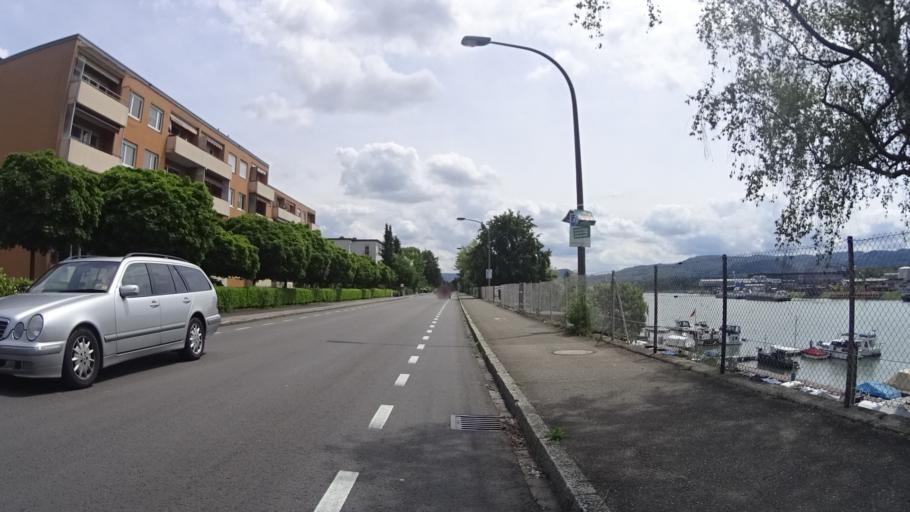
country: CH
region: Basel-Landschaft
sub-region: Bezirk Arlesheim
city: Birsfelden
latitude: 47.5603
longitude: 7.6395
